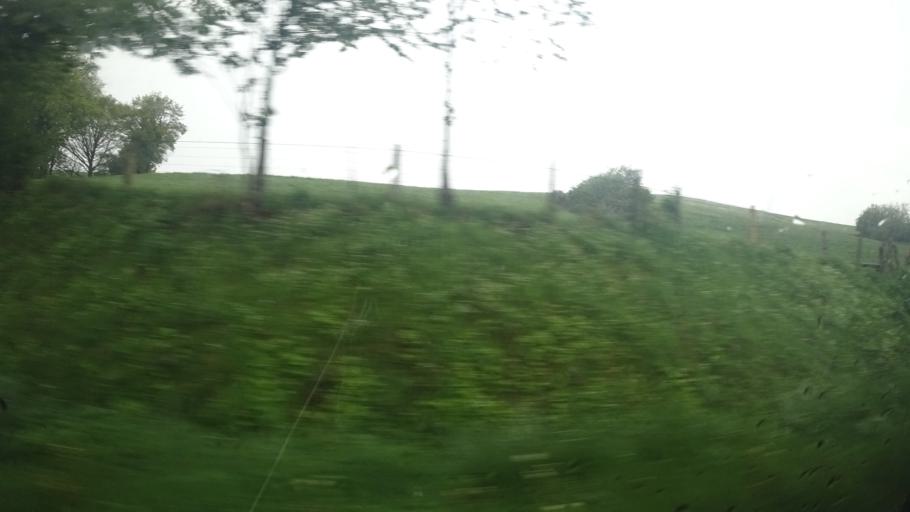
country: FR
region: Midi-Pyrenees
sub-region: Departement de l'Aveyron
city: Laissac
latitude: 44.3204
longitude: 2.7965
